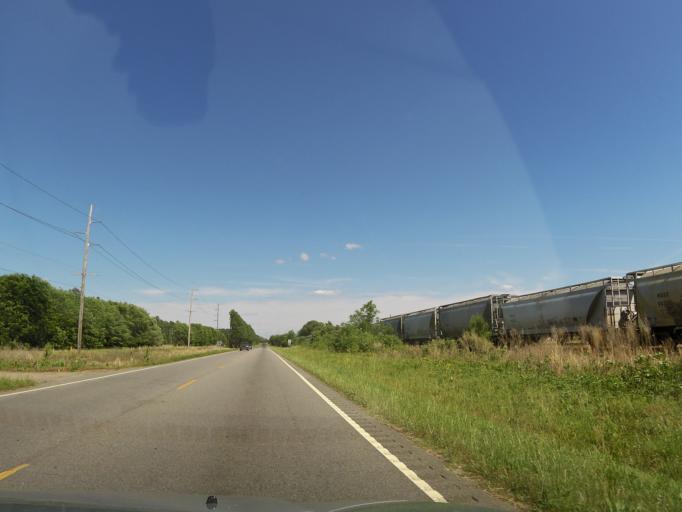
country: US
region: South Carolina
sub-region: Aiken County
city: Aiken
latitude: 33.5419
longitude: -81.6681
